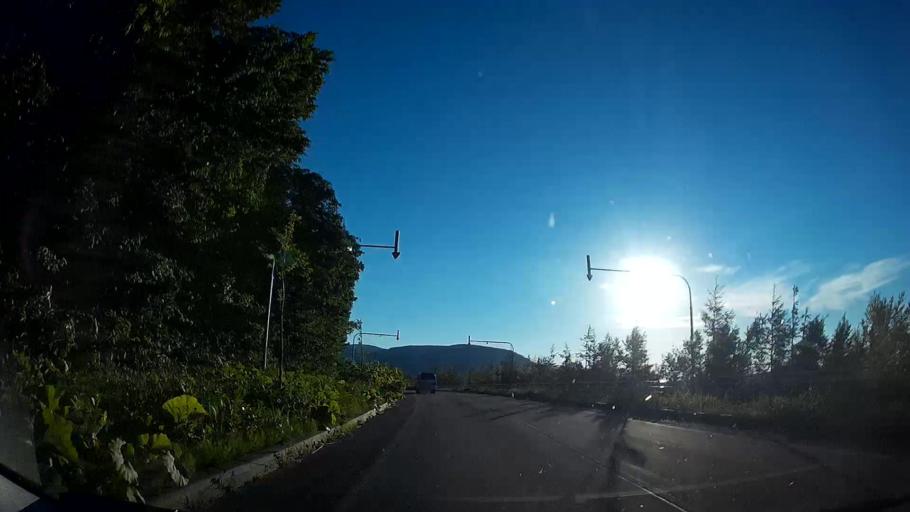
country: JP
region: Hokkaido
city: Otaru
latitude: 43.1676
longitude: 141.0194
